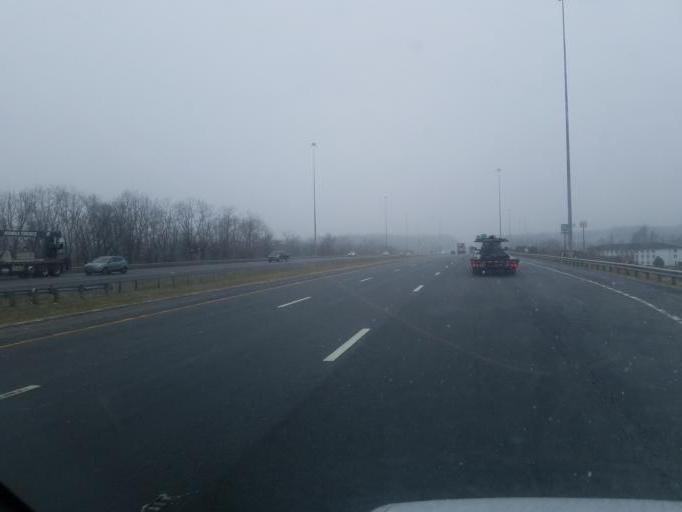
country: US
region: Ohio
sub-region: Sandusky County
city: Bellville
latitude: 40.6444
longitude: -82.5471
